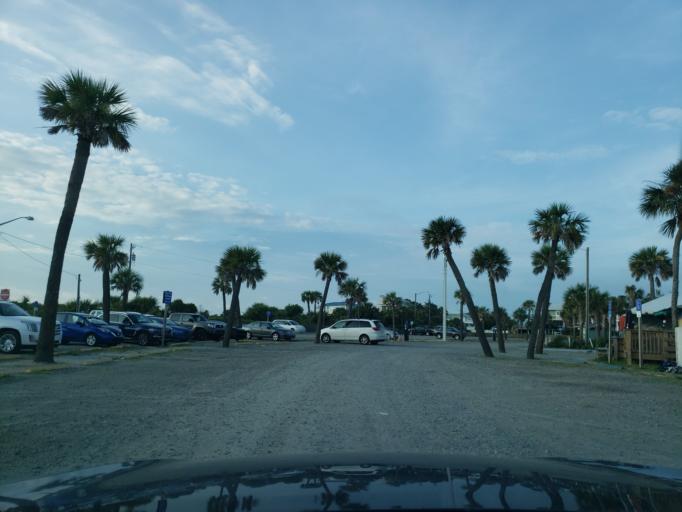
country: US
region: Georgia
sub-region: Chatham County
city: Tybee Island
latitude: 32.0221
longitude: -80.8436
